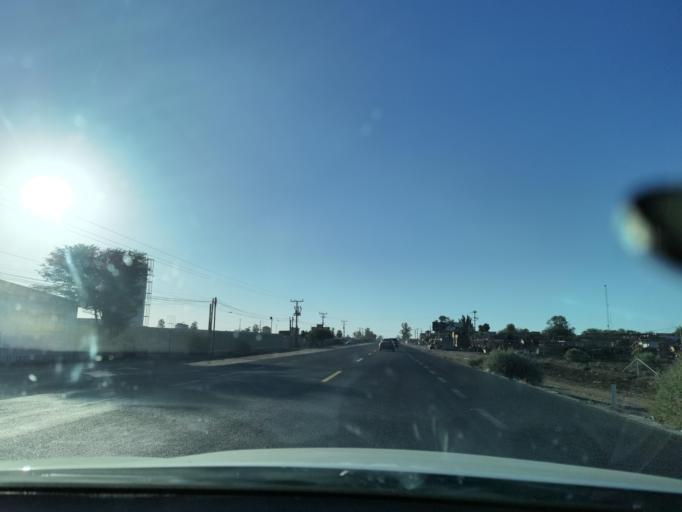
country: MX
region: Baja California
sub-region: Mexicali
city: Islas Agrarias Grupo A
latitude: 32.6480
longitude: -115.3306
